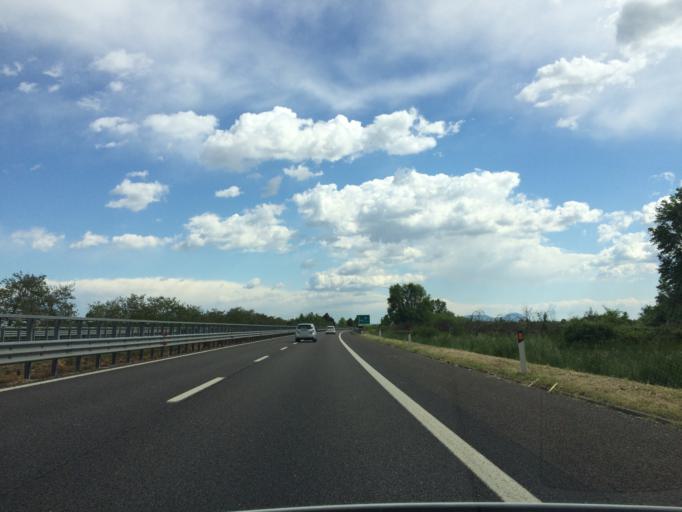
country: IT
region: Veneto
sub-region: Provincia di Vicenza
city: Lisiera
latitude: 45.5695
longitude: 11.6105
